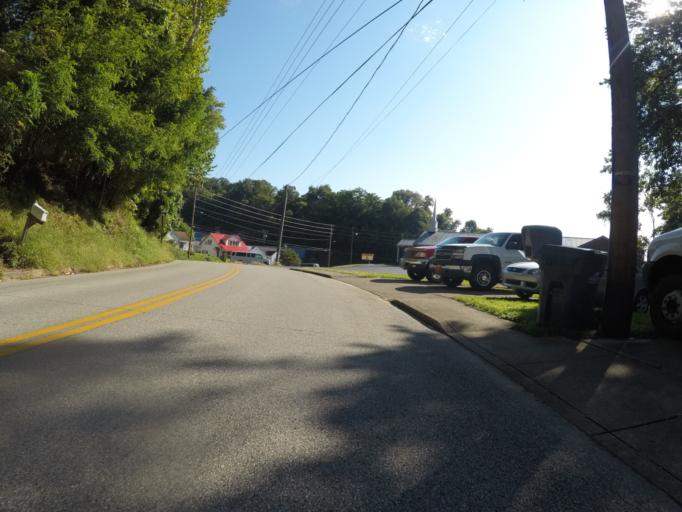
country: US
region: Kentucky
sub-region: Boyd County
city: Ashland
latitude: 38.4552
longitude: -82.6164
